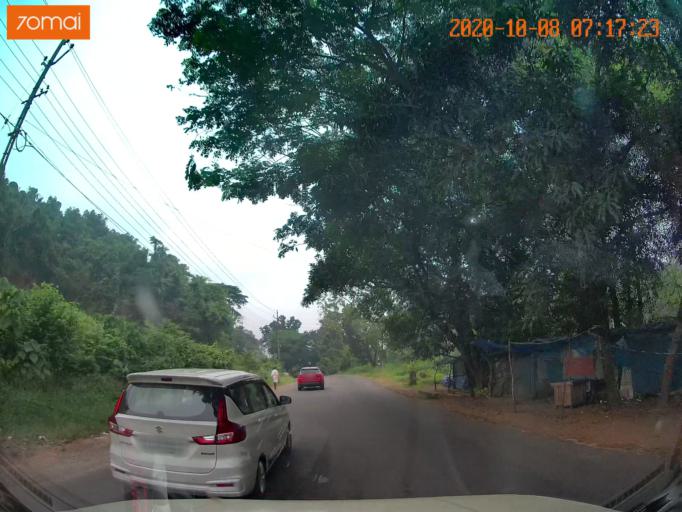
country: IN
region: Kerala
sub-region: Malappuram
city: Ponnani
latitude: 10.8367
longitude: 76.0184
